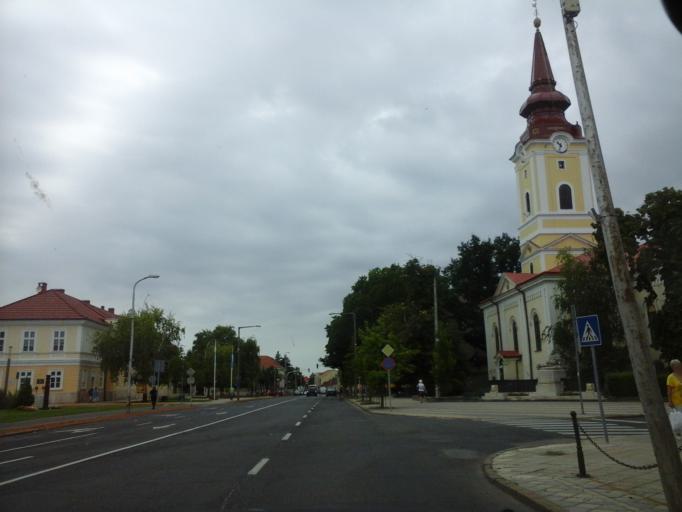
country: HU
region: Hajdu-Bihar
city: Hajduszoboszlo
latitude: 47.4438
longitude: 21.3897
